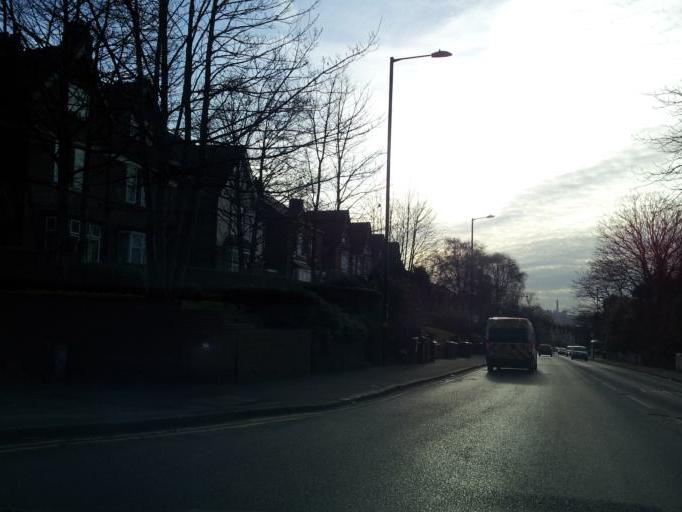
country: GB
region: England
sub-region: City and Borough of Birmingham
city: Birmingham
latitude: 52.5124
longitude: -1.8523
